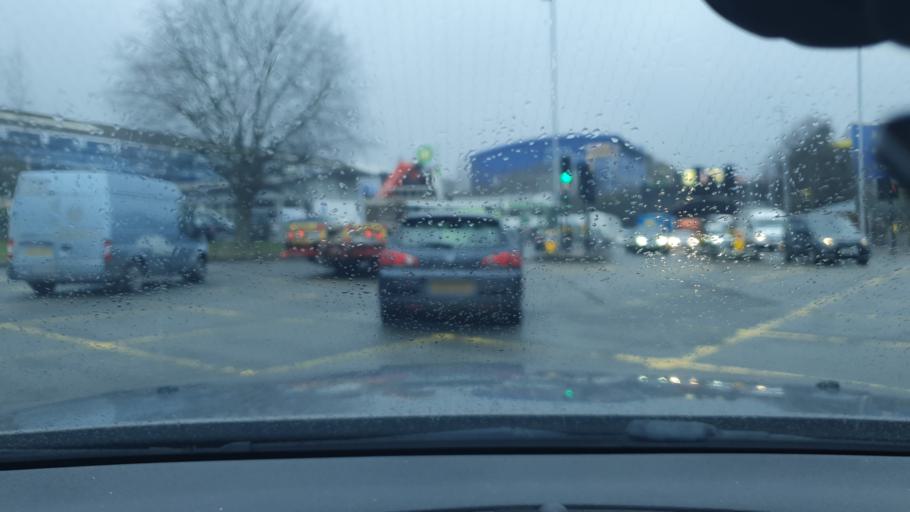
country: GB
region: England
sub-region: Greater London
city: Wood Green
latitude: 51.6113
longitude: -0.1353
